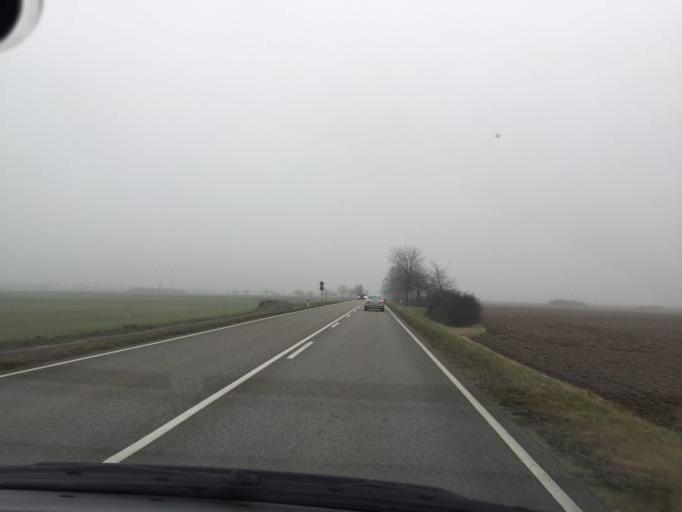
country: DE
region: Baden-Wuerttemberg
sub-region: Freiburg Region
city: Hartheim
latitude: 47.9775
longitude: 7.6484
